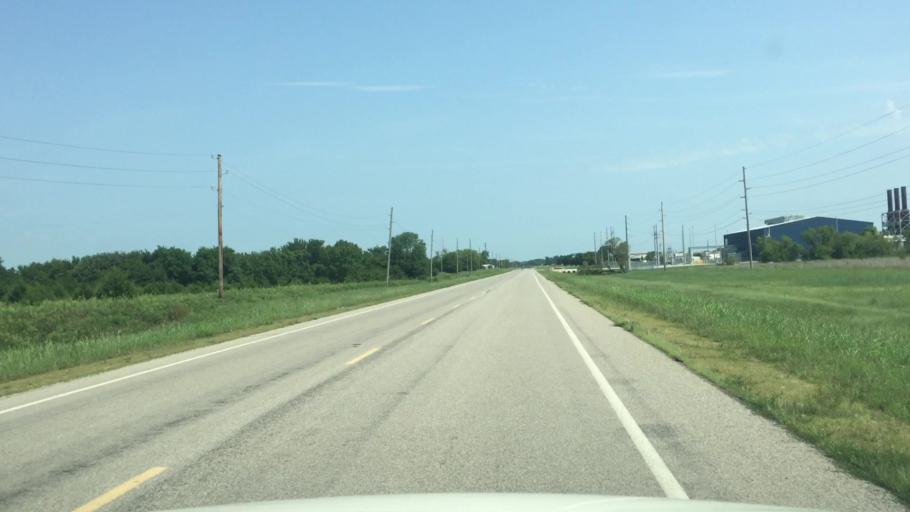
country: US
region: Kansas
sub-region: Montgomery County
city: Coffeyville
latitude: 37.0899
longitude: -95.5862
